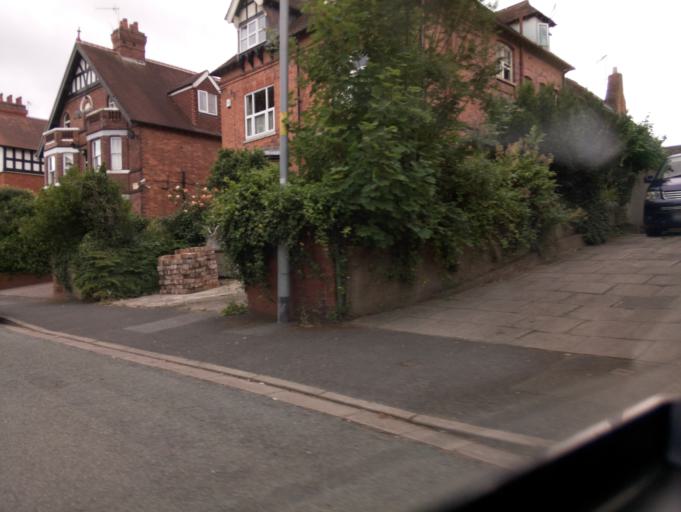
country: GB
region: England
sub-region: Worcestershire
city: Worcester
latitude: 52.1828
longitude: -2.2181
